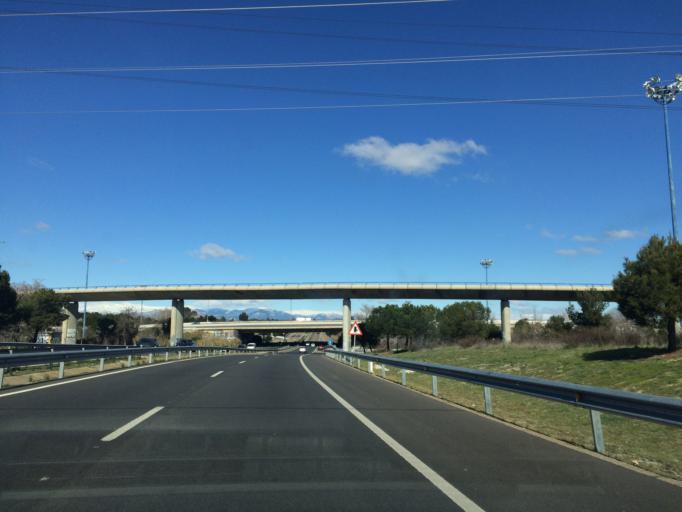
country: ES
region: Madrid
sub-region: Provincia de Madrid
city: Las Tablas
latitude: 40.5171
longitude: -3.6857
